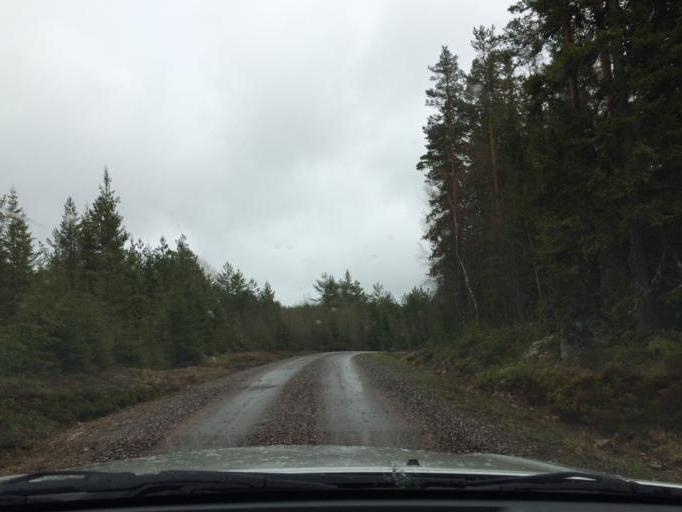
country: SE
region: OErebro
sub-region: Hallefors Kommun
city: Haellefors
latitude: 60.0307
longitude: 14.5525
